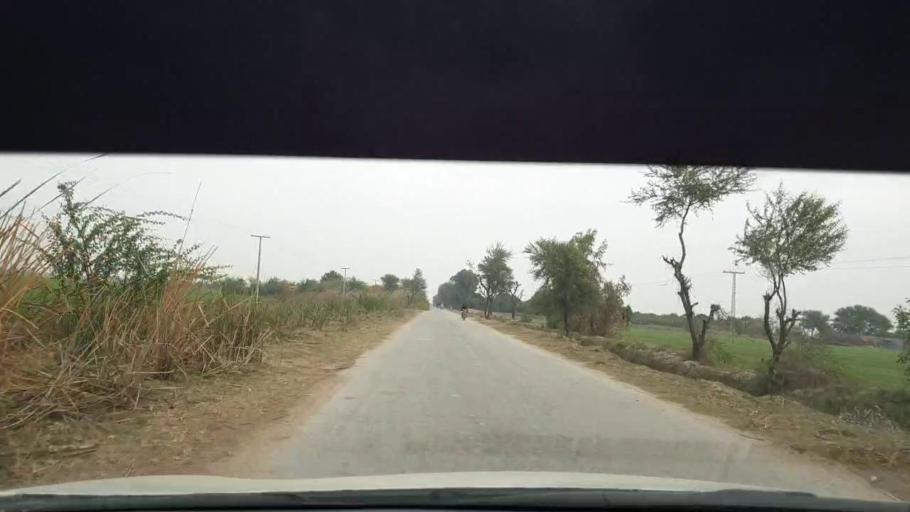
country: PK
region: Sindh
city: Berani
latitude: 25.7761
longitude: 68.8667
